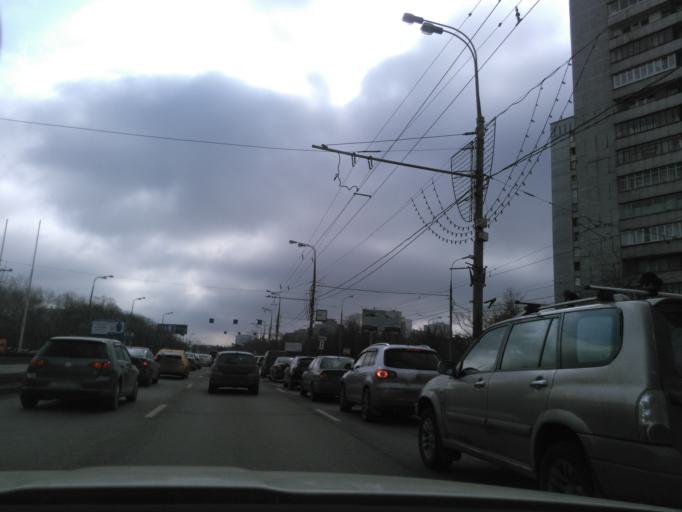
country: RU
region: Moscow
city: Pokrovskoye-Streshnevo
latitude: 55.8146
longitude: 37.4691
